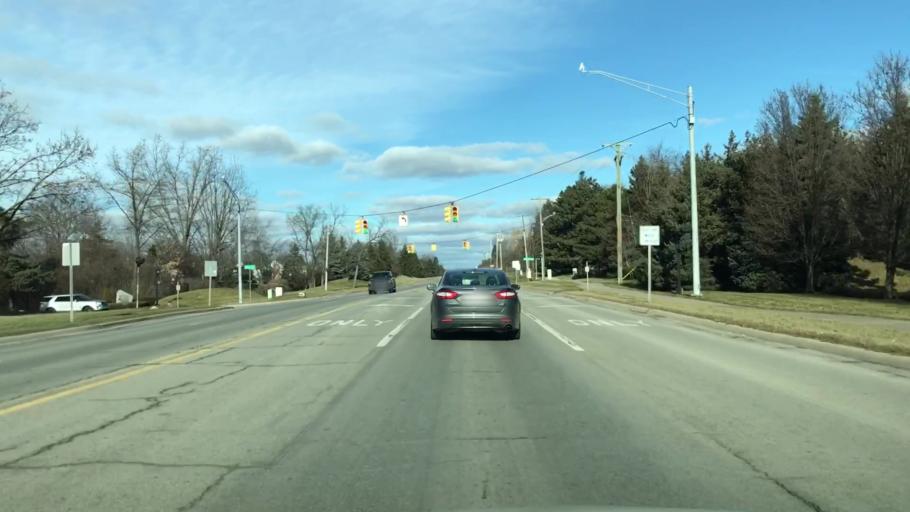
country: US
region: Michigan
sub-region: Oakland County
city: Auburn Hills
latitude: 42.6859
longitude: -83.1942
